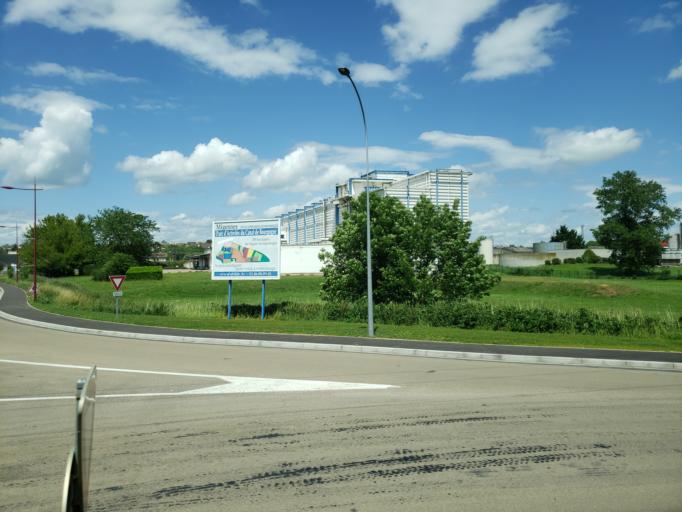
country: FR
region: Bourgogne
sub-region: Departement de l'Yonne
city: Migennes
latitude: 47.9568
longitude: 3.5052
